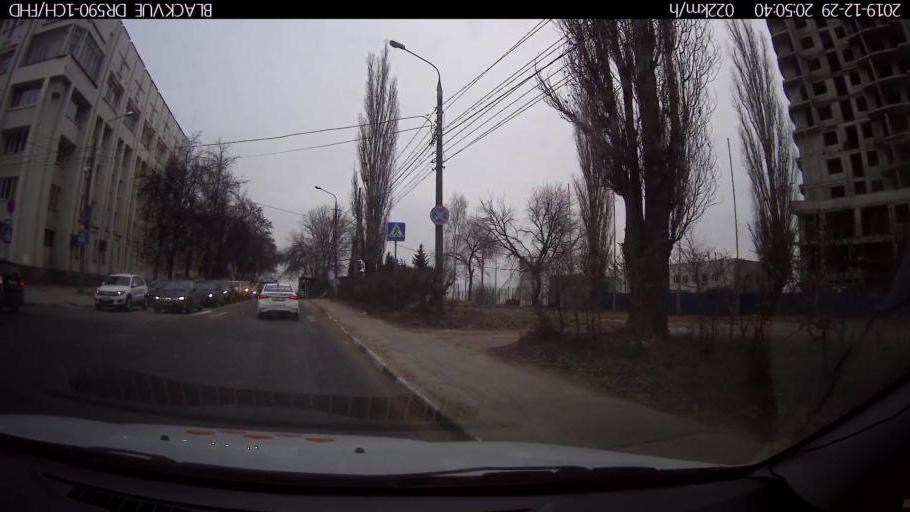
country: RU
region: Nizjnij Novgorod
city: Nizhniy Novgorod
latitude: 56.3197
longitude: 44.0329
